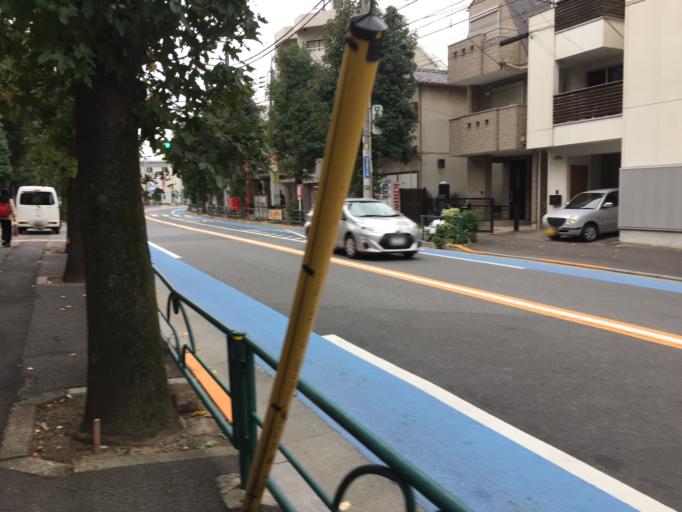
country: JP
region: Tokyo
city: Tokyo
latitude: 35.6518
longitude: 139.6709
